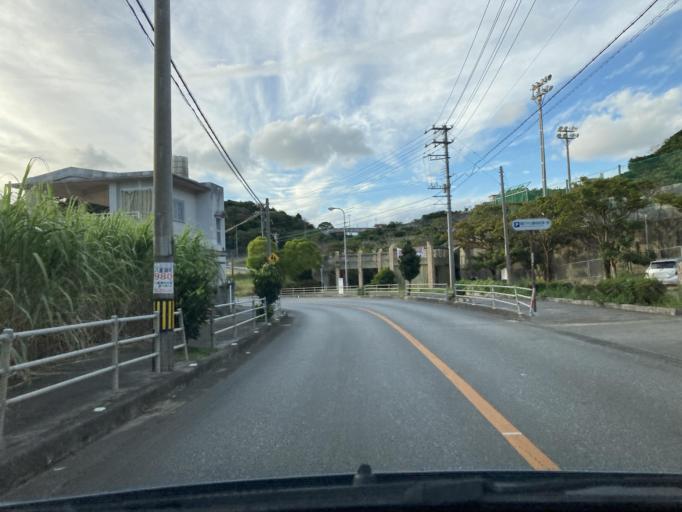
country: JP
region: Okinawa
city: Tomigusuku
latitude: 26.1515
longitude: 127.7045
